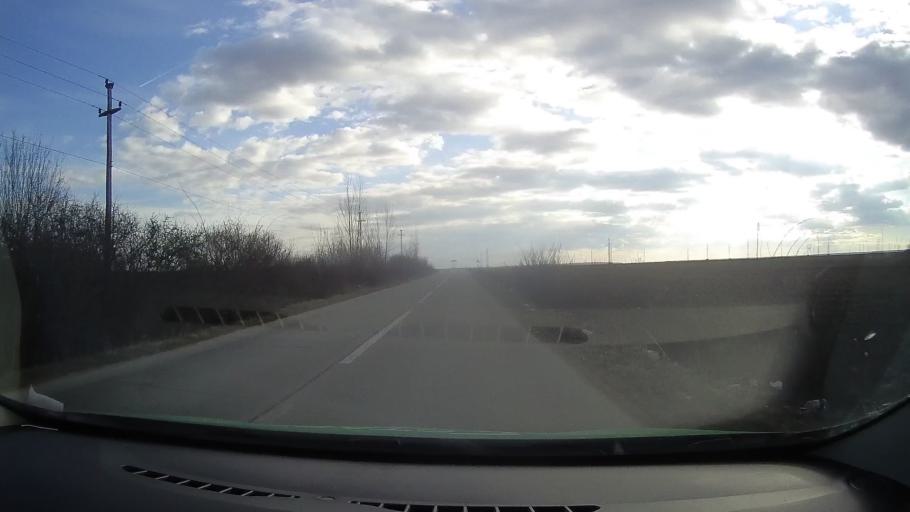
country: RO
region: Dambovita
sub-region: Comuna Ulmi
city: Ulmi
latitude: 44.8867
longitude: 25.4647
